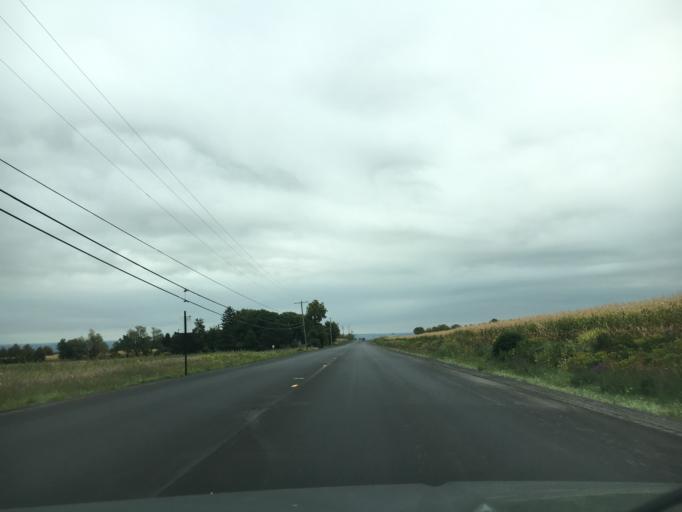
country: US
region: New York
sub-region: Cayuga County
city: Union Springs
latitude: 42.6812
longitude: -76.8076
